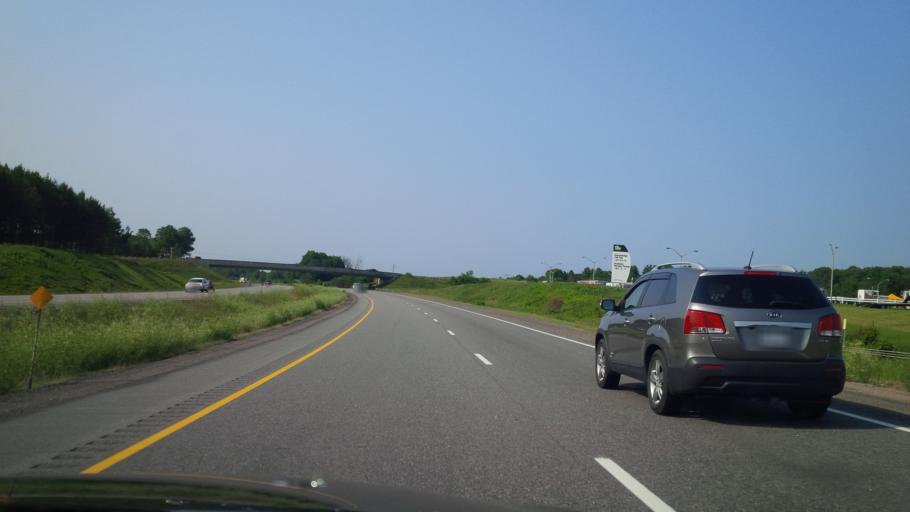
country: CA
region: Ontario
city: Bracebridge
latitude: 45.0378
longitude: -79.2917
